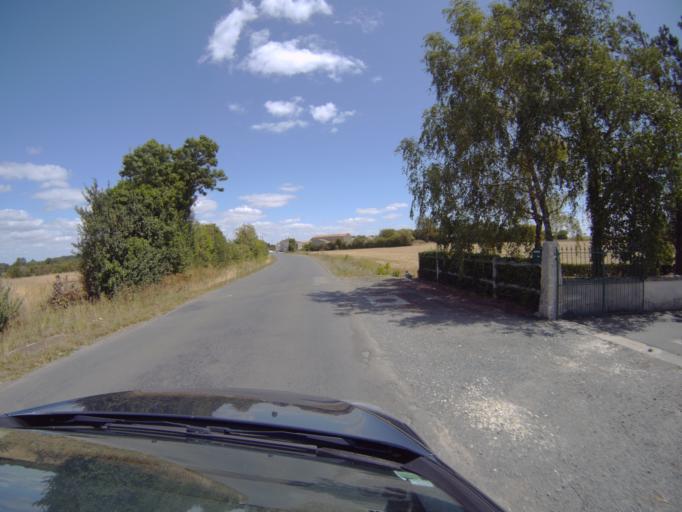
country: FR
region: Poitou-Charentes
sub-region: Departement de la Charente-Maritime
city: Courcon
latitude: 46.2477
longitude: -0.7924
